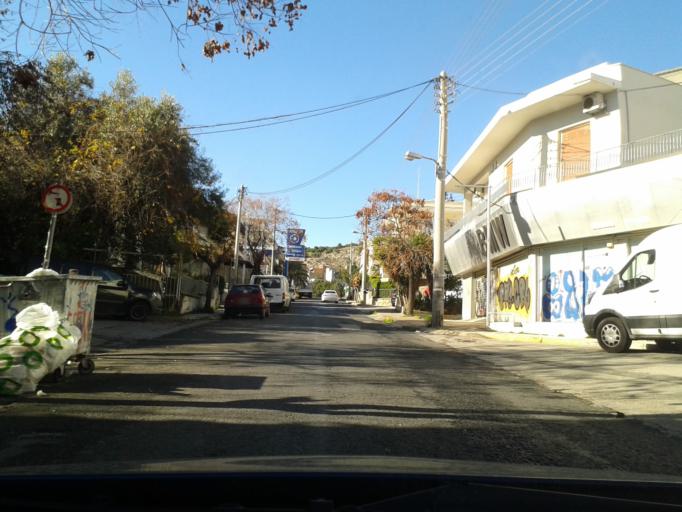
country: GR
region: Attica
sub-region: Nomarchia Athinas
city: Psychiko
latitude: 38.0012
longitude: 23.7639
